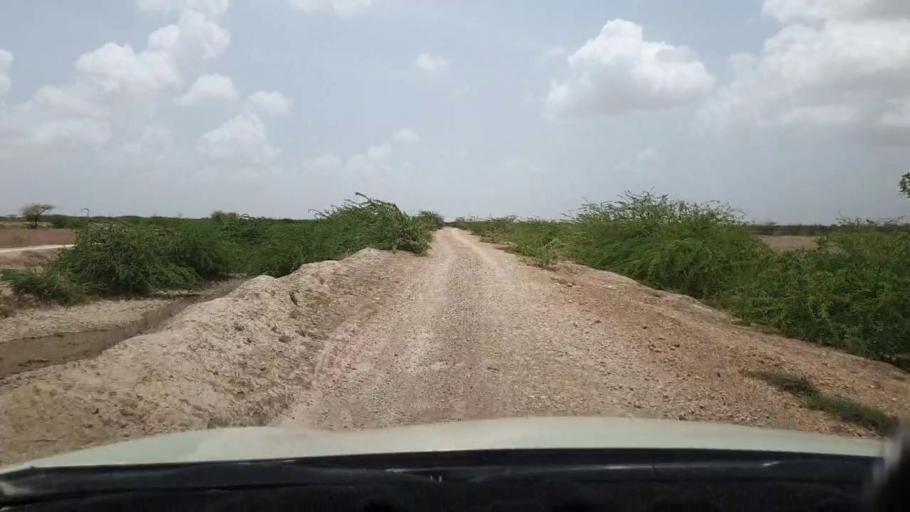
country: PK
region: Sindh
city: Kadhan
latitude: 24.3573
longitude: 68.9249
